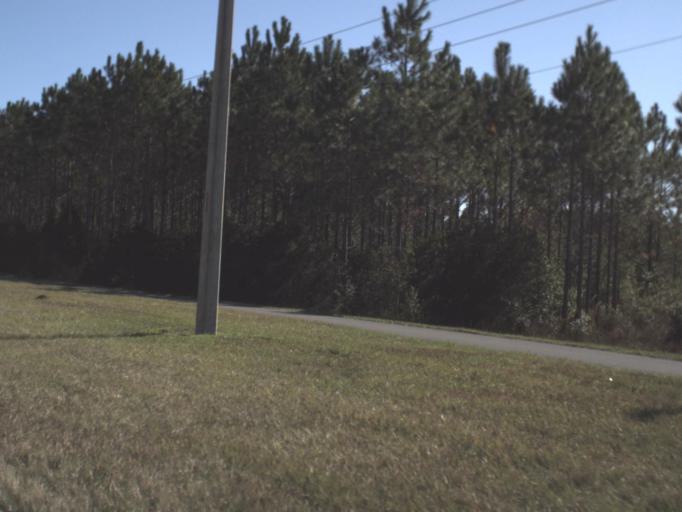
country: US
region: Florida
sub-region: Flagler County
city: Palm Coast
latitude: 29.6026
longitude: -81.2706
